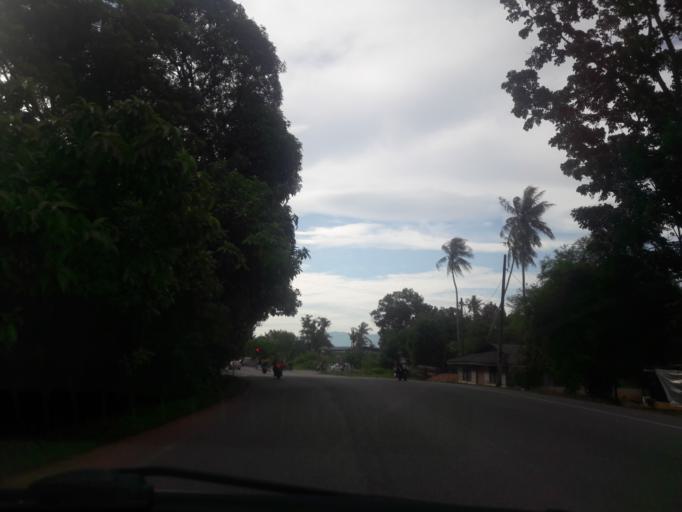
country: MY
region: Kedah
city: Sungai Petani
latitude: 5.6321
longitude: 100.5188
